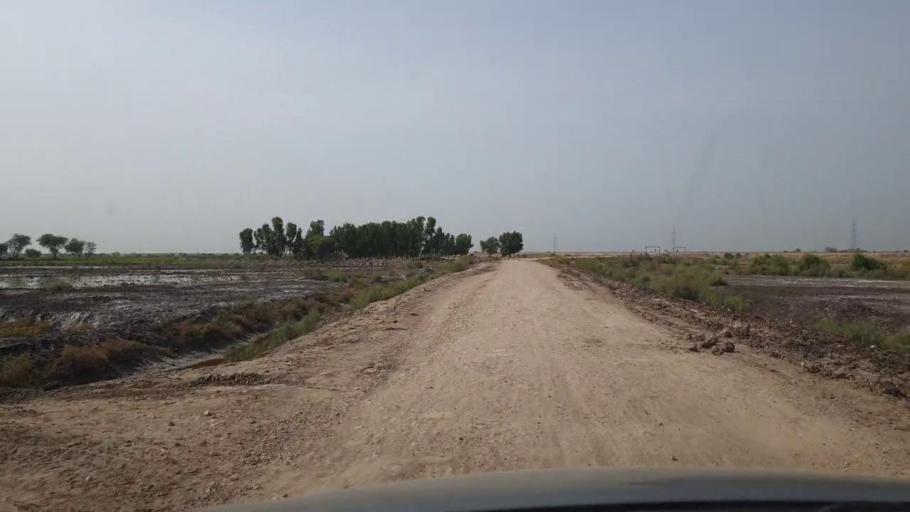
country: PK
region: Sindh
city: Lakhi
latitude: 27.8351
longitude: 68.6998
